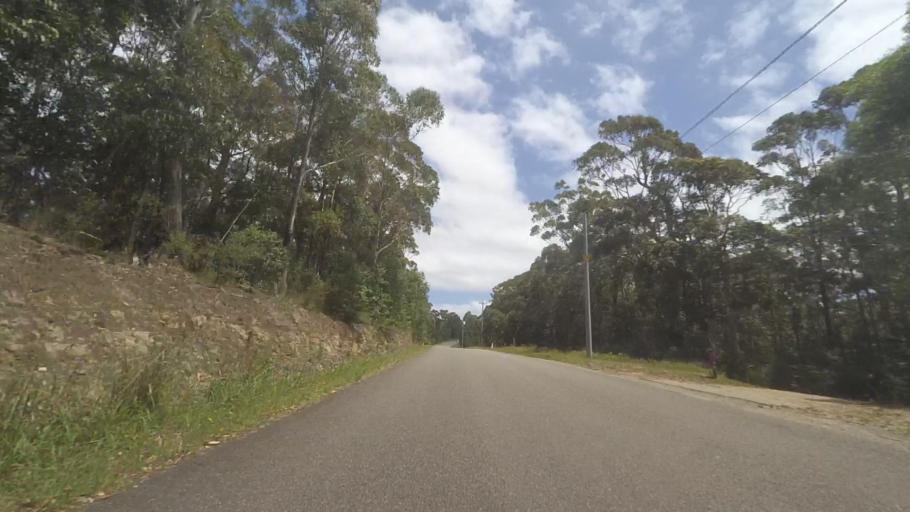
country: AU
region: New South Wales
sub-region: Shoalhaven Shire
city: Milton
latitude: -35.4085
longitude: 150.3567
